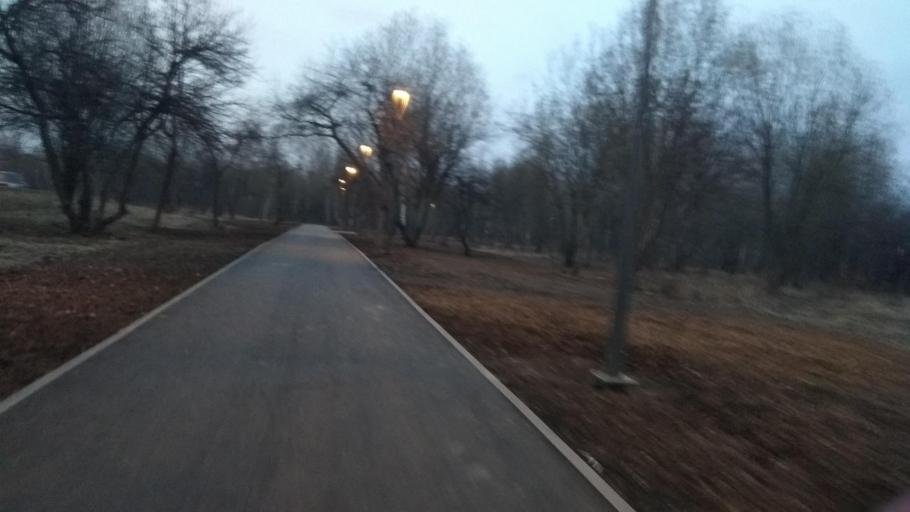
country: RU
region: Moscow
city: Biryulevo
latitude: 55.5829
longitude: 37.6981
